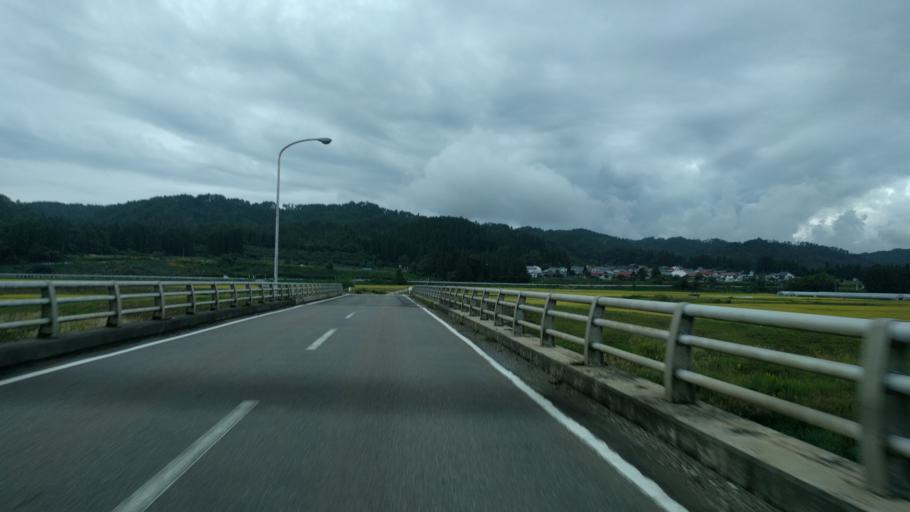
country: JP
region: Fukushima
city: Kitakata
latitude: 37.6133
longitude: 139.8363
